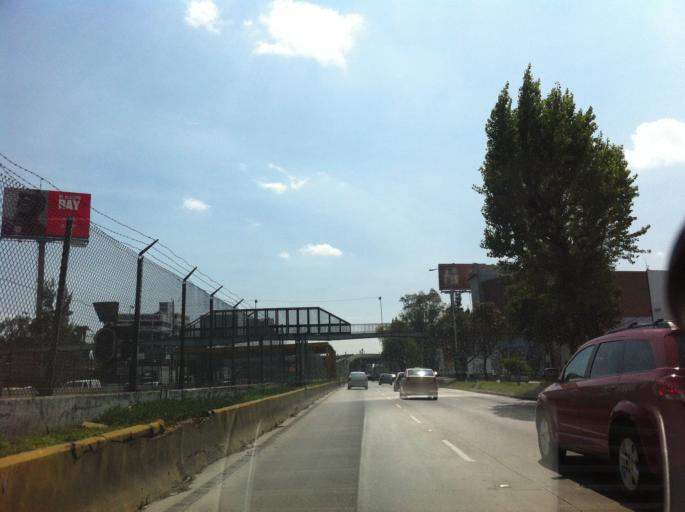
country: MX
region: Mexico City
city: Venustiano Carranza
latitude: 19.4574
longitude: -99.1165
